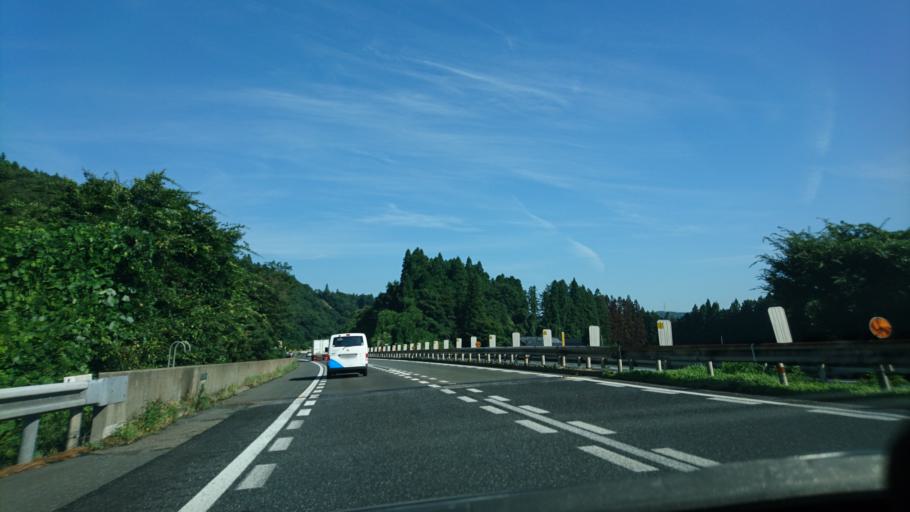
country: JP
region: Iwate
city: Ichinoseki
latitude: 39.0015
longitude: 141.0891
